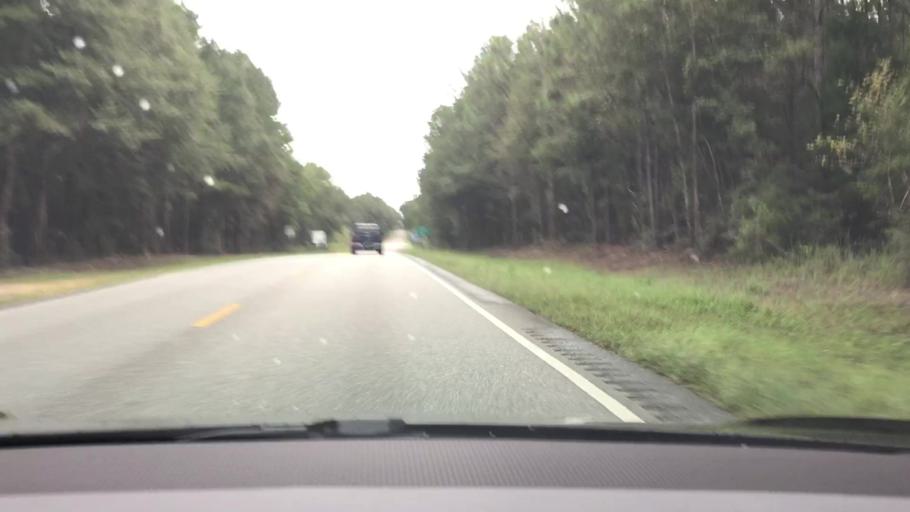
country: US
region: Alabama
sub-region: Geneva County
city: Samson
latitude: 30.9943
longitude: -86.1327
